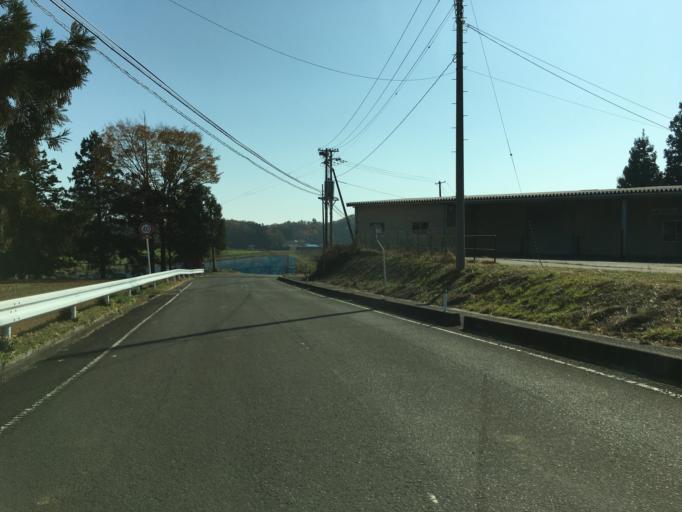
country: JP
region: Fukushima
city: Nihommatsu
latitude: 37.5791
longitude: 140.3929
